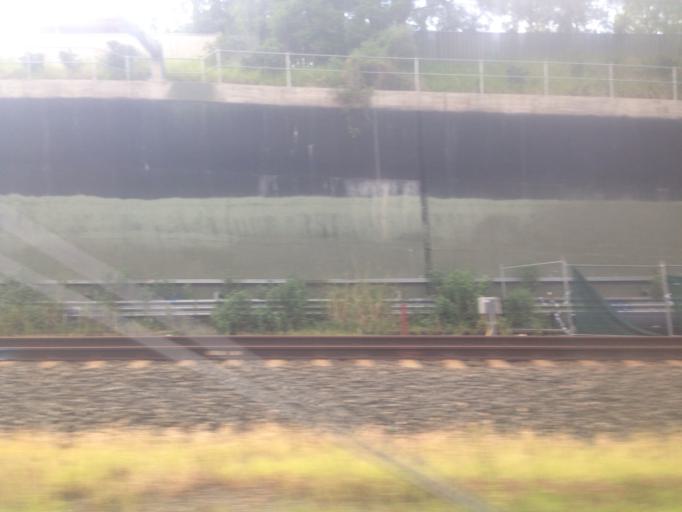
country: AU
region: New South Wales
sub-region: Willoughby
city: Chatswood
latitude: -33.8034
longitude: 151.1812
